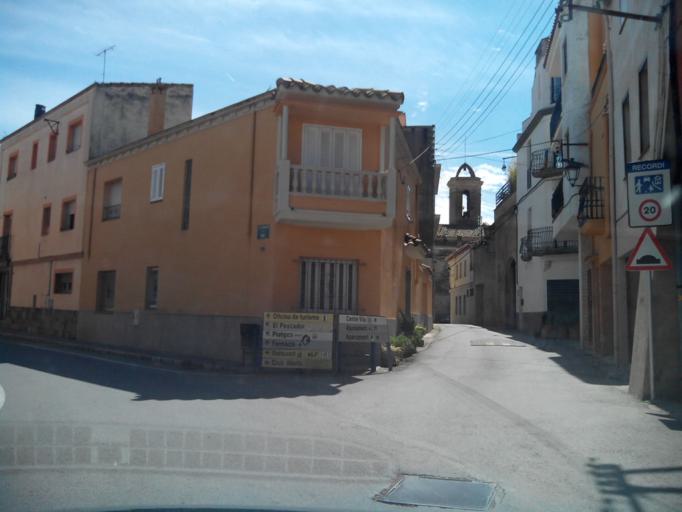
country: ES
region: Catalonia
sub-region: Provincia de Girona
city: Sant Pere Pescador
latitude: 42.1895
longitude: 3.0820
